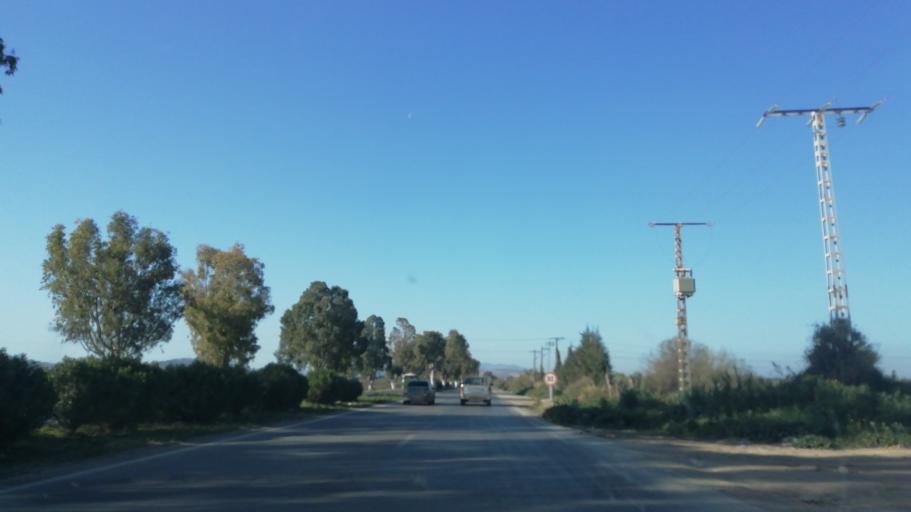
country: DZ
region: Mascara
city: Mascara
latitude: 35.6089
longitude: 0.0957
